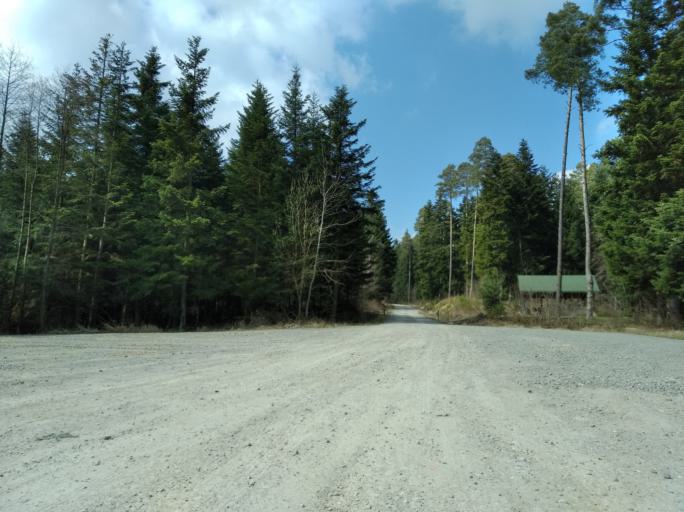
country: PL
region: Subcarpathian Voivodeship
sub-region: Powiat strzyzowski
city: Strzyzow
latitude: 49.8121
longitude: 21.8262
